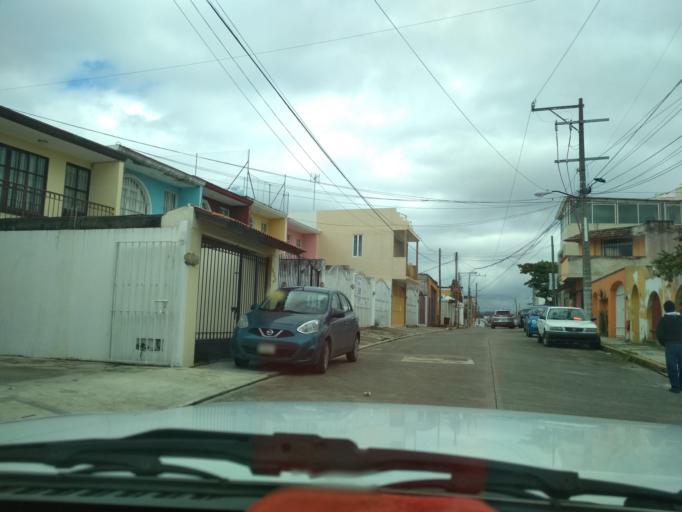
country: MX
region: Veracruz
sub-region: Xalapa
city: Xalapa de Enriquez
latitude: 19.5068
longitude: -96.9258
